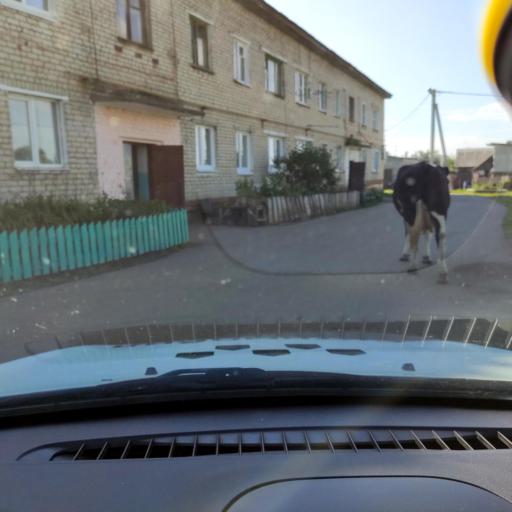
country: RU
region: Samara
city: Tol'yatti
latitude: 53.3530
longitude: 49.2941
